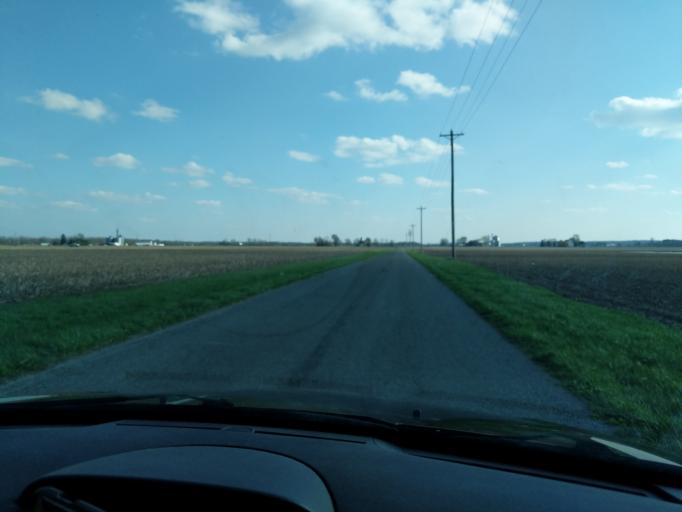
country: US
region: Ohio
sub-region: Champaign County
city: Urbana
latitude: 40.1180
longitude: -83.8081
